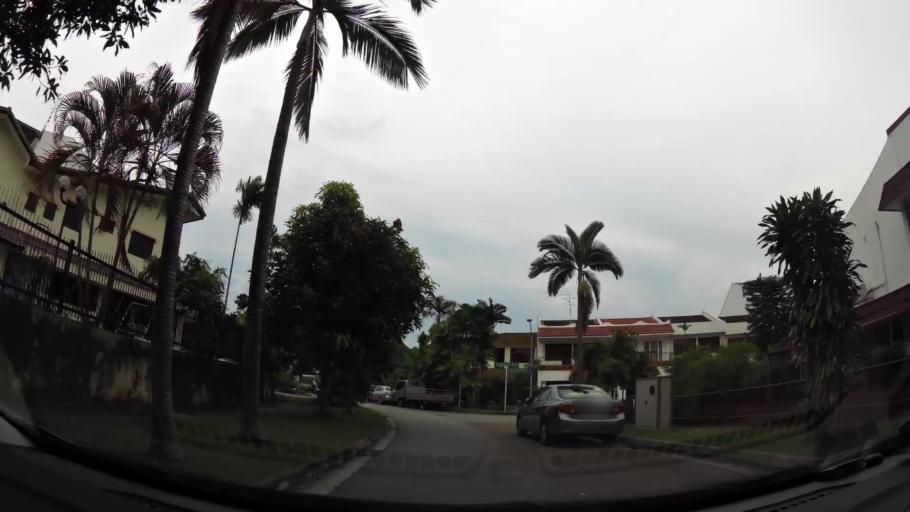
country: SG
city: Singapore
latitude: 1.3614
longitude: 103.8816
